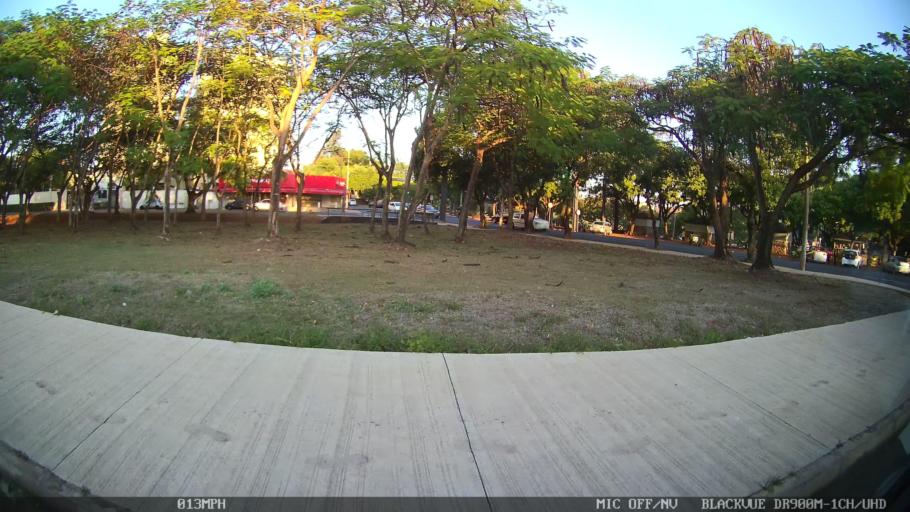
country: BR
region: Sao Paulo
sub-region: Sao Jose Do Rio Preto
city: Sao Jose do Rio Preto
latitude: -20.8064
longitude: -49.3614
